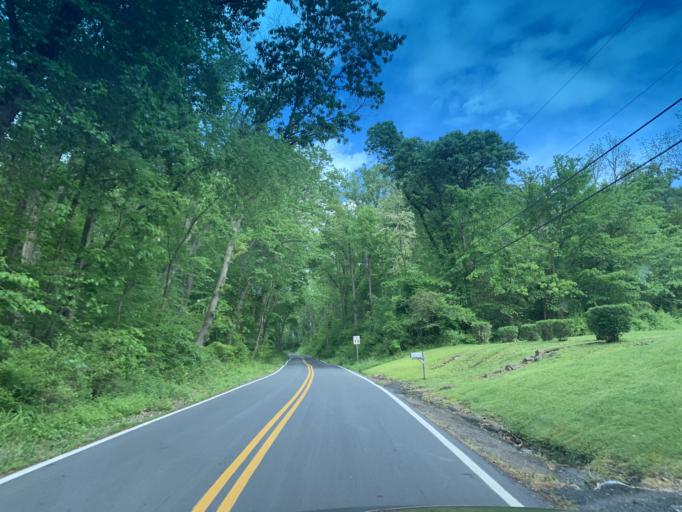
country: US
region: Maryland
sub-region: Cecil County
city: Rising Sun
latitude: 39.6827
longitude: -76.1924
